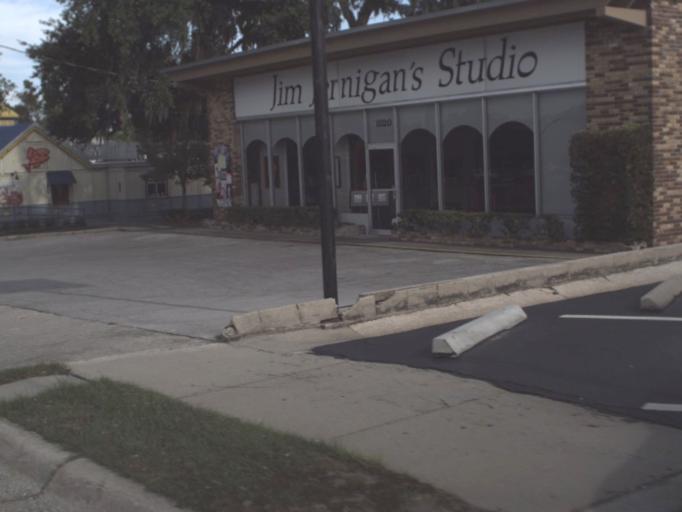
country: US
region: Florida
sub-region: Marion County
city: Ocala
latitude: 29.1869
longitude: -82.1133
